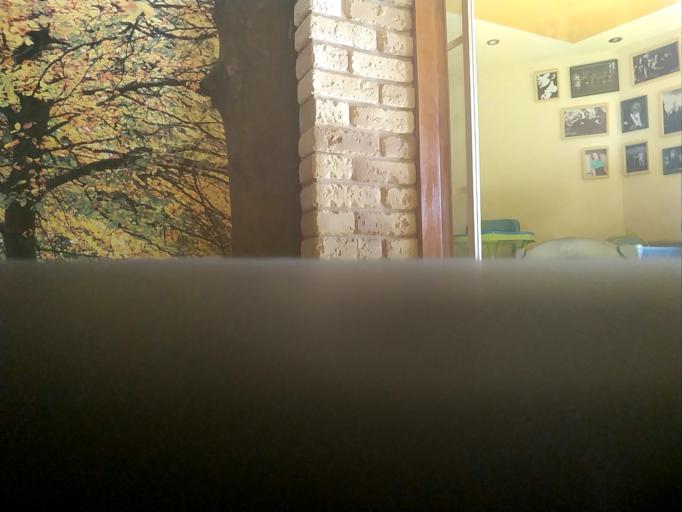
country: RU
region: Smolensk
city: Temkino
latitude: 55.0238
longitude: 34.9286
